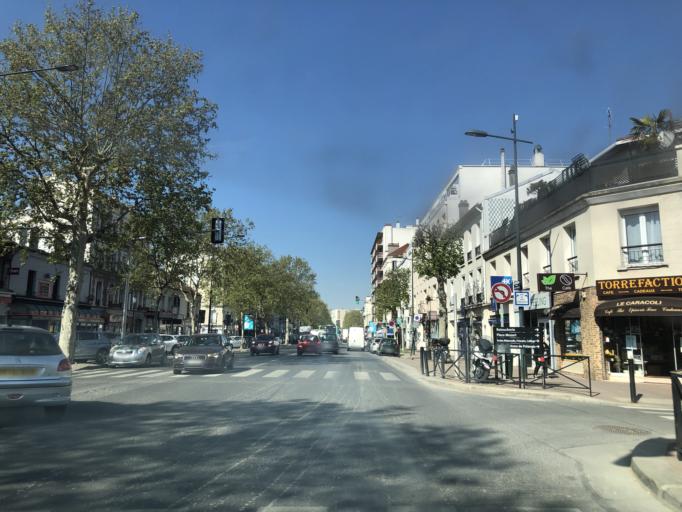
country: FR
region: Ile-de-France
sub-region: Departement du Val-de-Marne
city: Joinville-le-Pont
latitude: 48.8201
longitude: 2.4787
